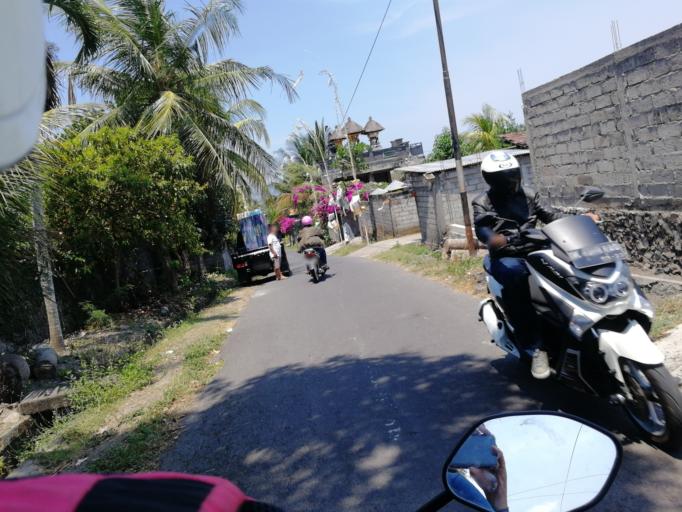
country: ID
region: Bali
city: Banjar Timbrah
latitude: -8.4664
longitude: 115.5928
